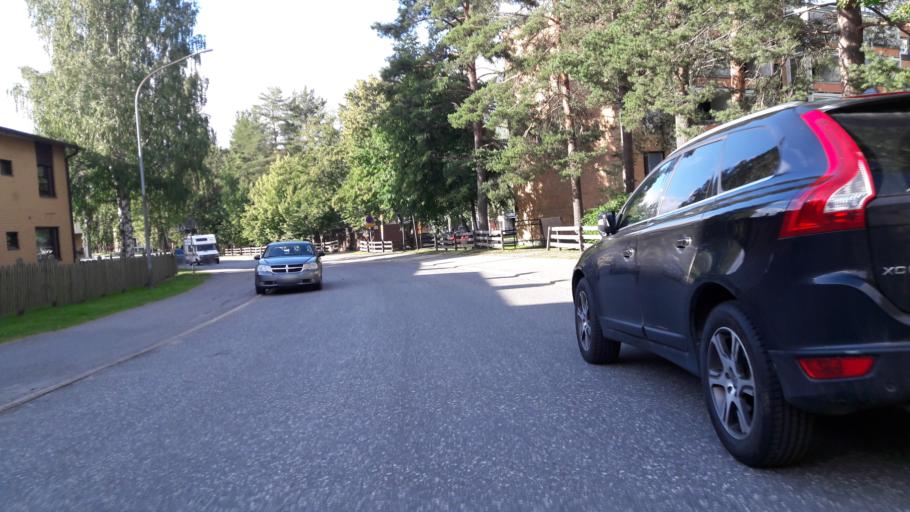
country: FI
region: North Karelia
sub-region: Joensuu
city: Joensuu
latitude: 62.6036
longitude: 29.8000
